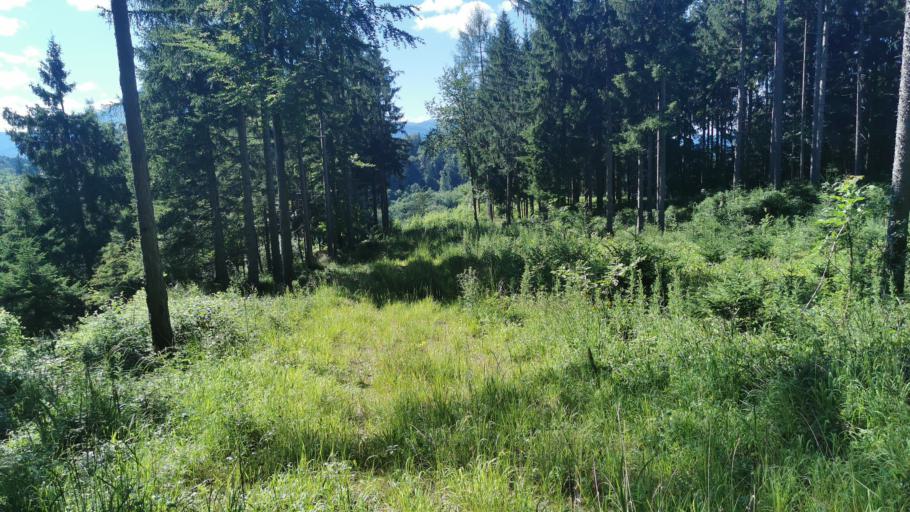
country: DE
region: Bavaria
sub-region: Upper Bavaria
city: Piding
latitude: 47.7316
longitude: 12.9490
